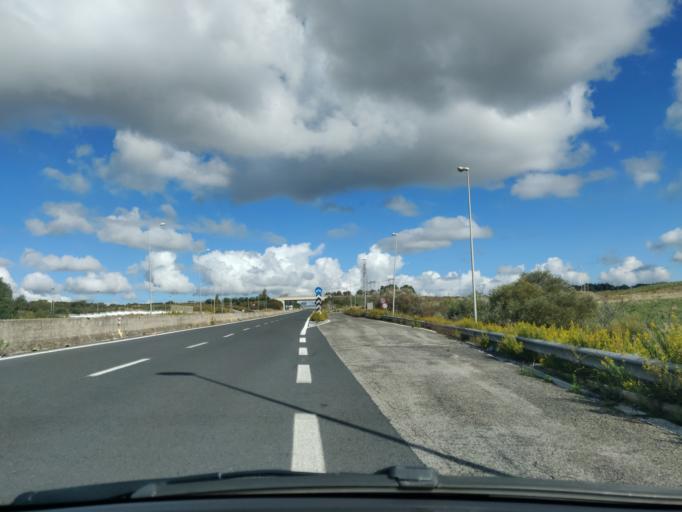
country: IT
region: Latium
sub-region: Citta metropolitana di Roma Capitale
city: Aurelia
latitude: 42.1269
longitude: 11.7909
